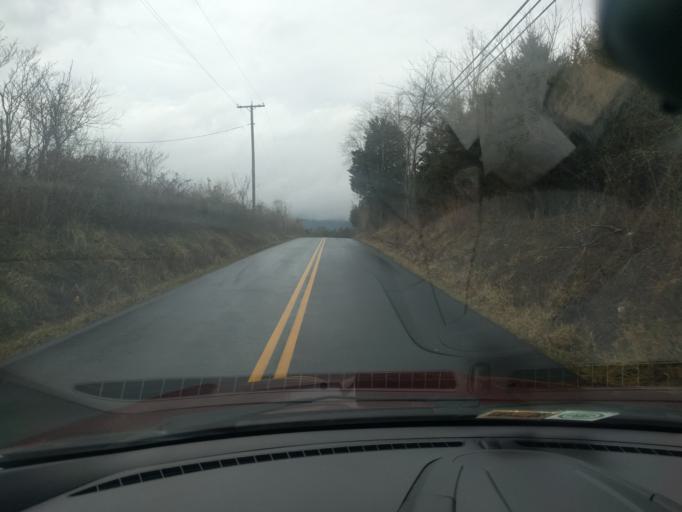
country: US
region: Virginia
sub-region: Botetourt County
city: Fincastle
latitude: 37.5226
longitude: -79.8811
